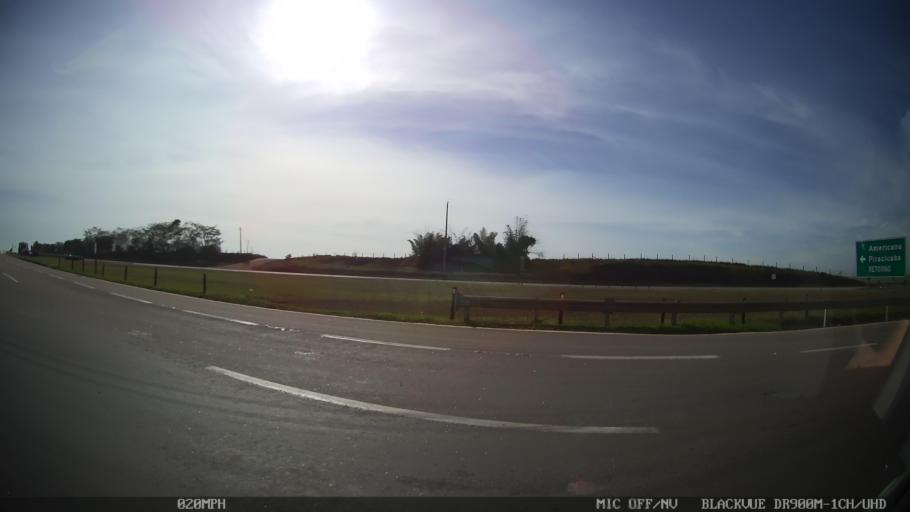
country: BR
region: Sao Paulo
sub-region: Rio Das Pedras
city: Rio das Pedras
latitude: -22.7943
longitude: -47.5818
